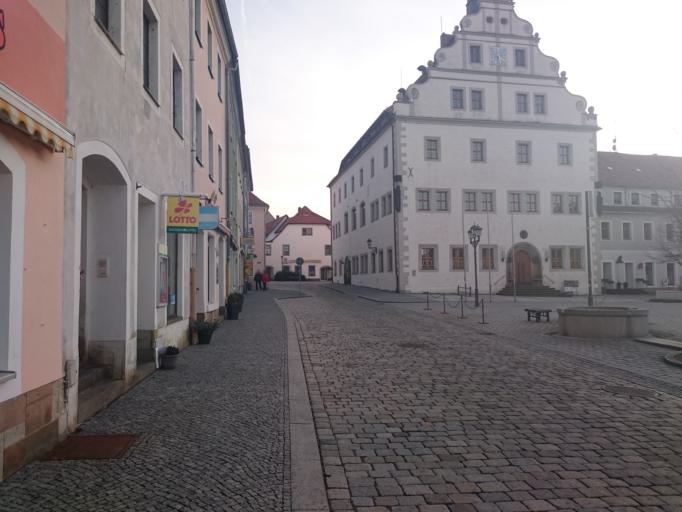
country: DE
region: Saxony
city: Dippoldiswalde
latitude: 50.8967
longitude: 13.6678
